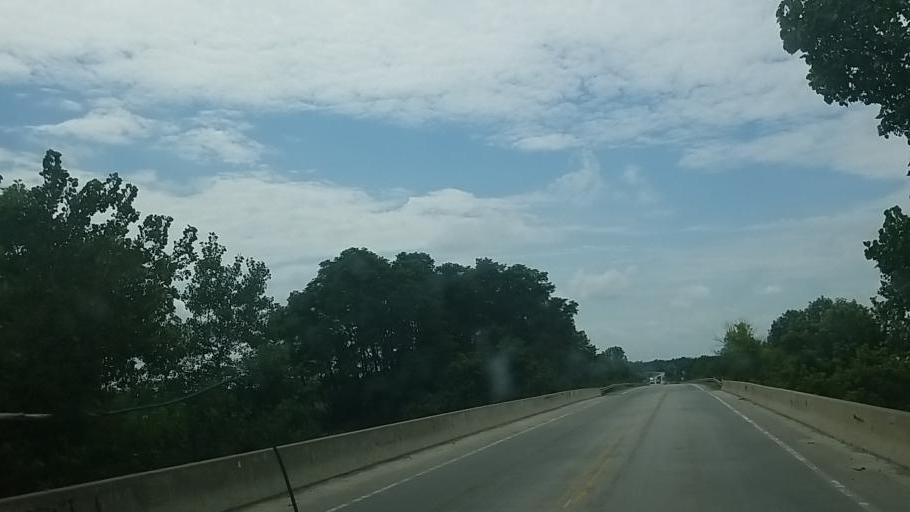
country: US
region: Ohio
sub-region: Franklin County
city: Obetz
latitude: 39.8313
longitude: -82.9549
